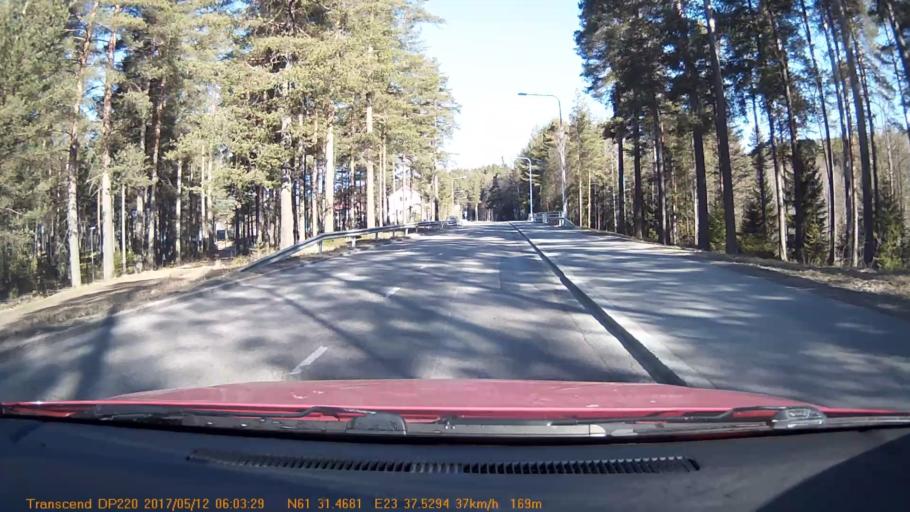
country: FI
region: Pirkanmaa
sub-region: Tampere
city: Yloejaervi
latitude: 61.5244
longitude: 23.6256
